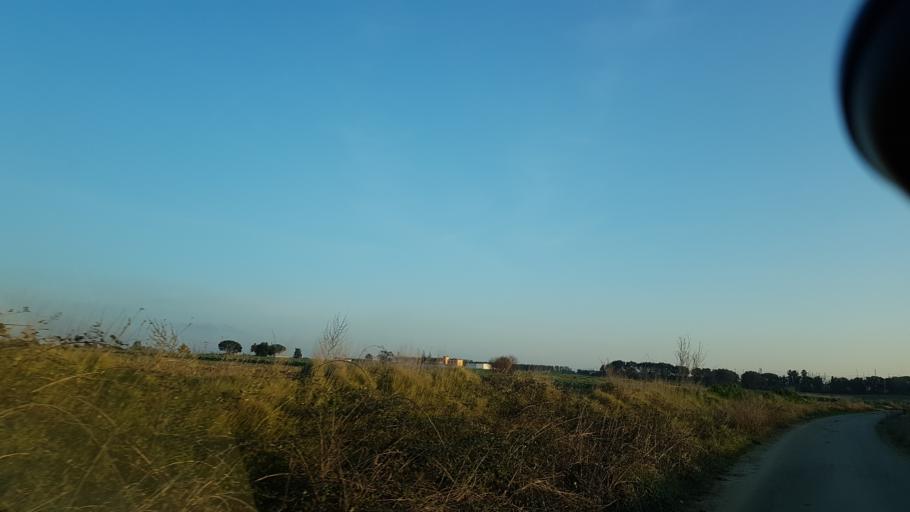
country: IT
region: Apulia
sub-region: Provincia di Brindisi
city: La Rosa
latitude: 40.6153
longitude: 17.9403
